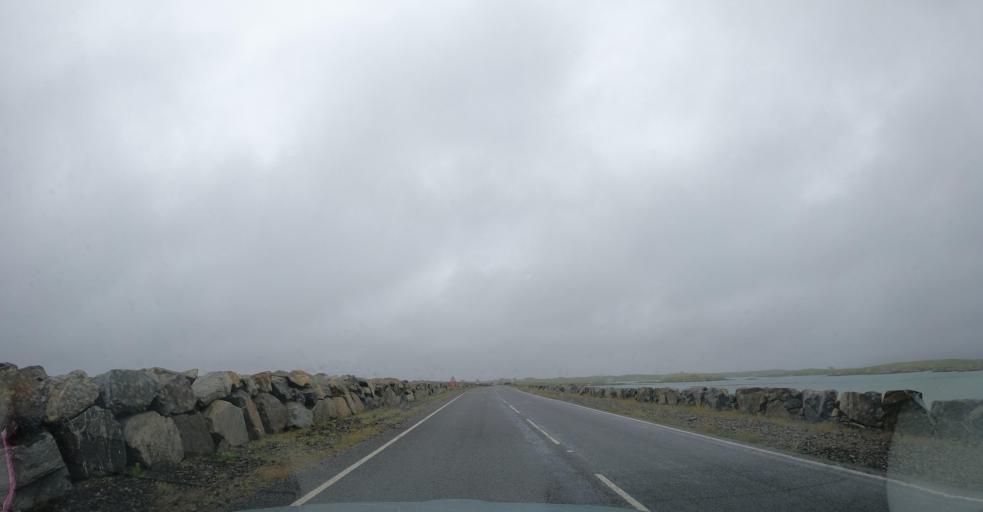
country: GB
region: Scotland
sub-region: Eilean Siar
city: Benbecula
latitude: 57.5016
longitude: -7.2634
